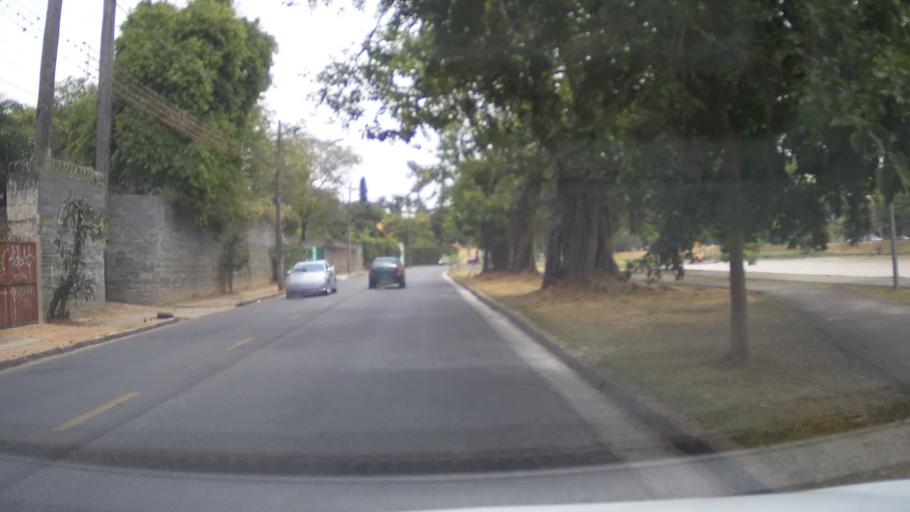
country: BR
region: Minas Gerais
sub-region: Belo Horizonte
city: Belo Horizonte
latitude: -19.8473
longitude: -43.9975
